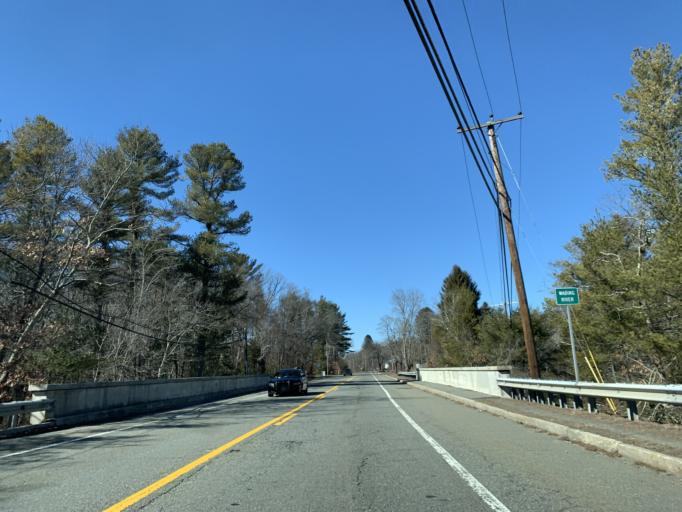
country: US
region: Massachusetts
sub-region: Bristol County
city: Norton
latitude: 41.9469
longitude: -71.1765
